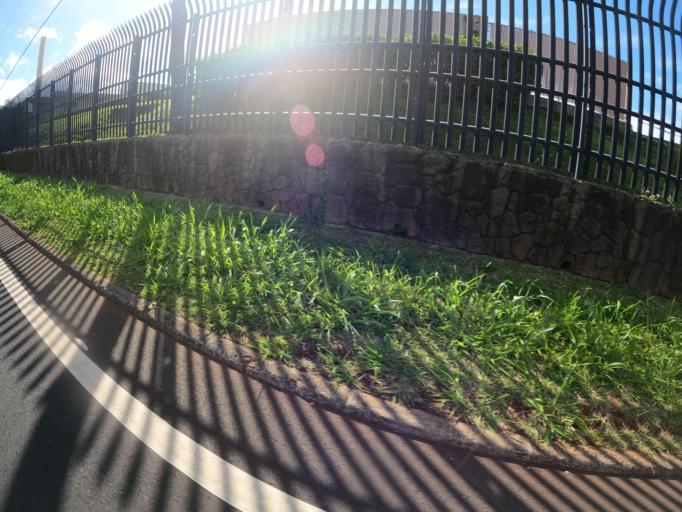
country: US
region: Hawaii
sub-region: Honolulu County
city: Halawa Heights
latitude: 21.3867
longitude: -157.9094
